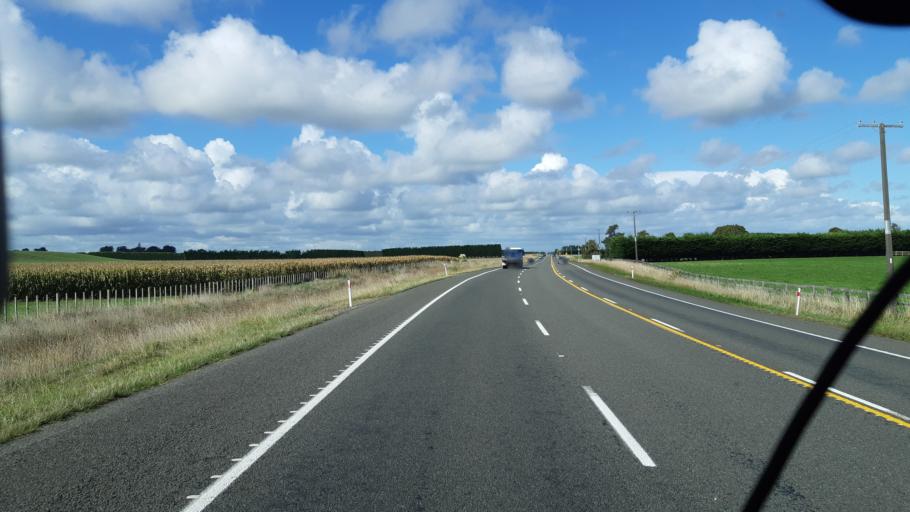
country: NZ
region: Manawatu-Wanganui
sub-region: Wanganui District
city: Wanganui
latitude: -39.9825
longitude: 175.1506
